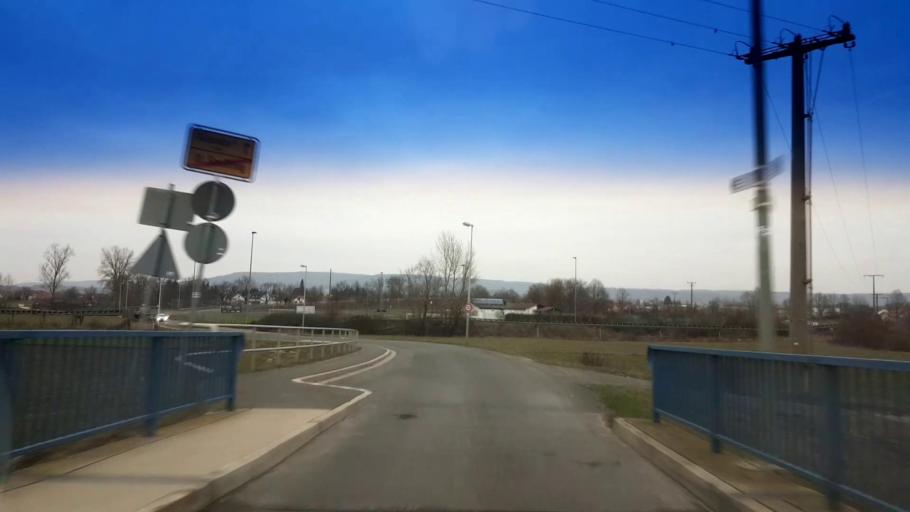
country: DE
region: Bavaria
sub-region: Upper Franconia
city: Altendorf
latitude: 49.7920
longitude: 11.0043
